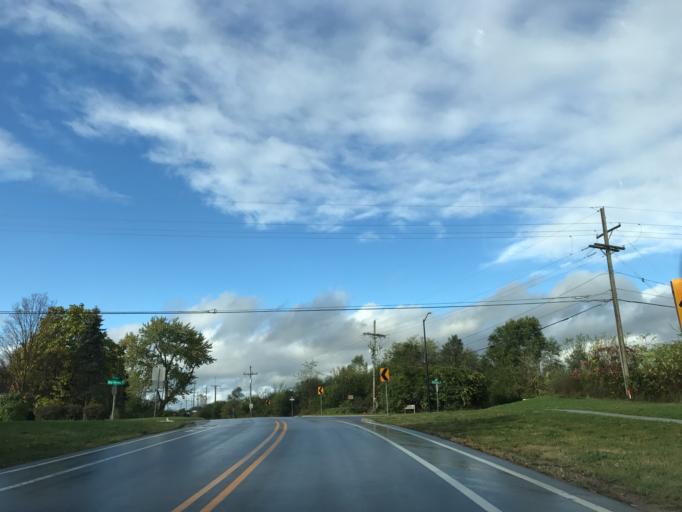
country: US
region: Michigan
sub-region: Washtenaw County
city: Ann Arbor
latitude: 42.3156
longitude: -83.7342
